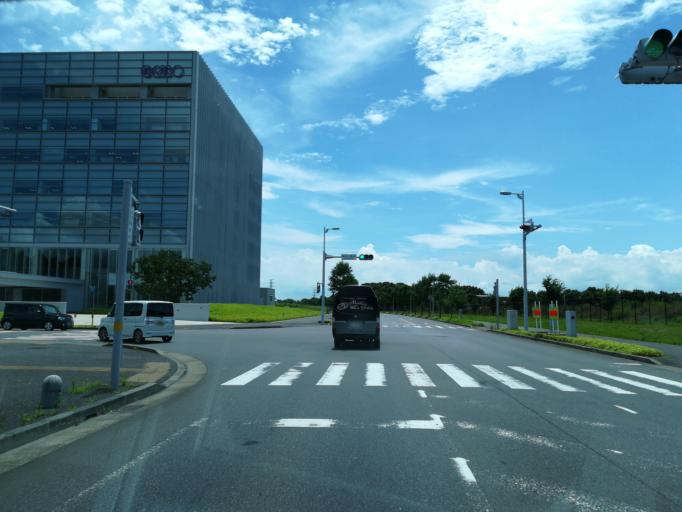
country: JP
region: Ibaraki
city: Naka
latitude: 36.0799
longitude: 140.0793
